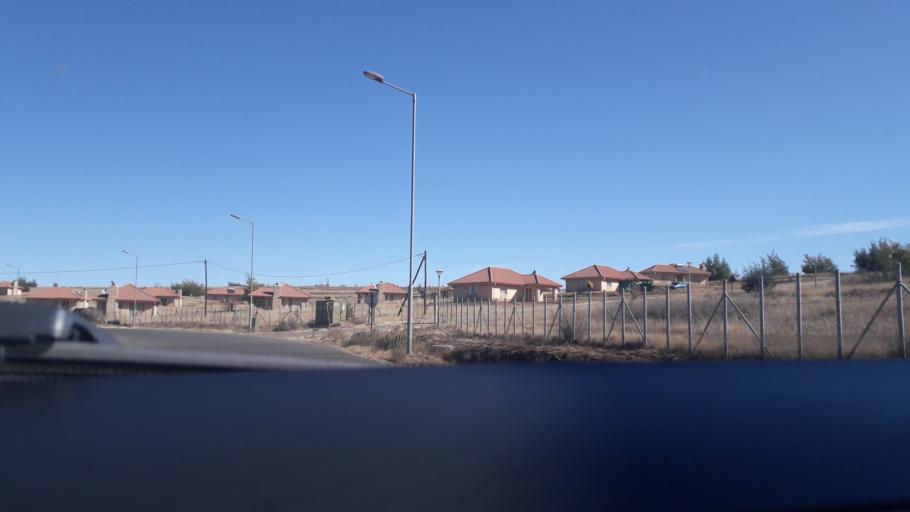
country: LS
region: Berea
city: Teyateyaneng
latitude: -29.3268
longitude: 27.7732
